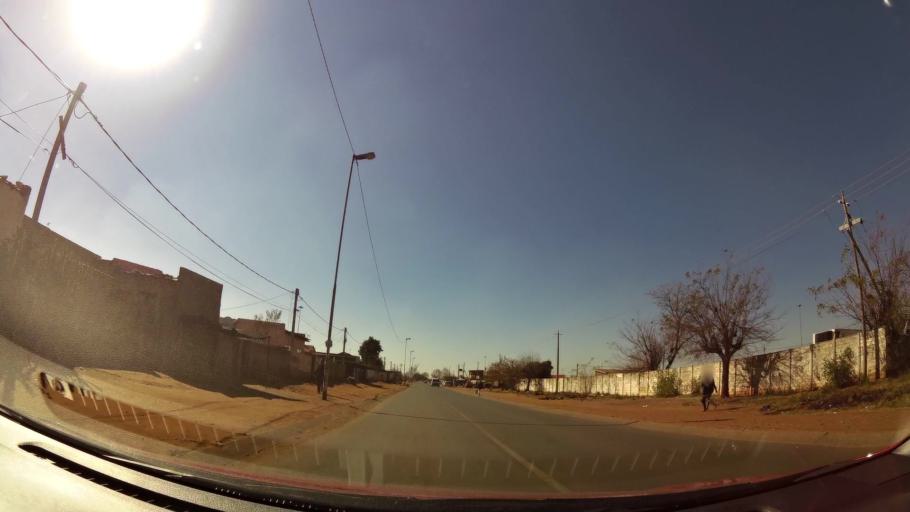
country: ZA
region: Gauteng
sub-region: City of Johannesburg Metropolitan Municipality
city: Soweto
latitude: -26.2239
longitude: 27.8308
